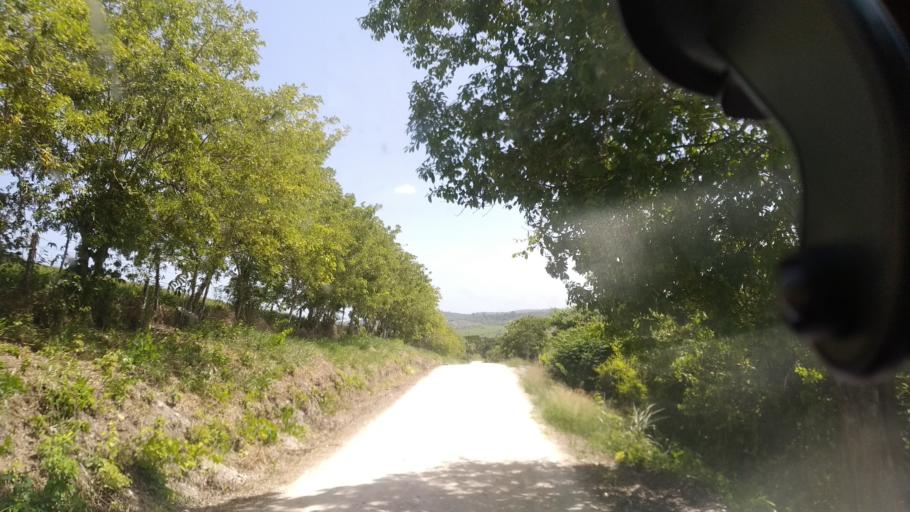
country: BZ
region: Cayo
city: San Ignacio
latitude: 17.2948
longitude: -89.0639
